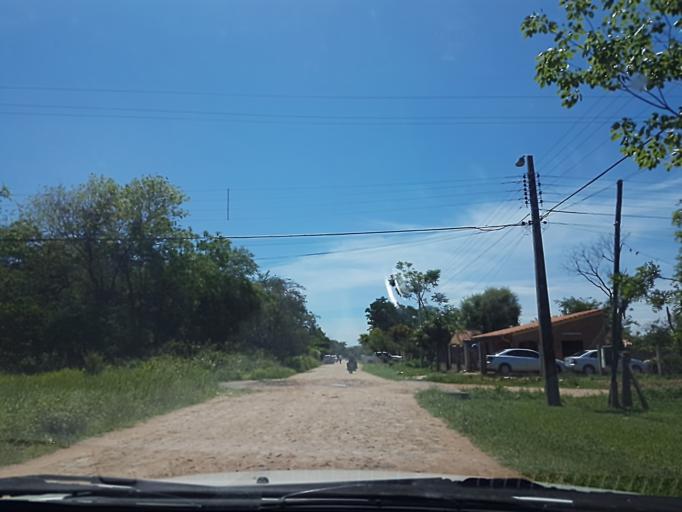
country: PY
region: Central
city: Limpio
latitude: -25.1857
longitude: -57.4867
